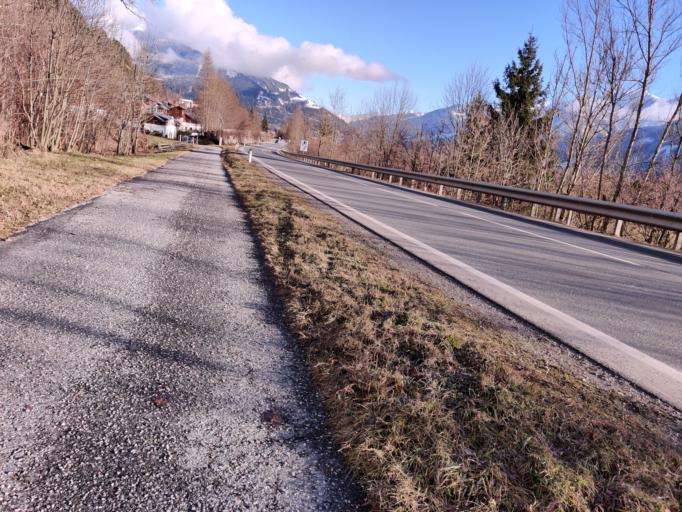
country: AT
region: Salzburg
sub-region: Politischer Bezirk Zell am See
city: Kaprun
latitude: 47.2953
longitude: 12.7677
